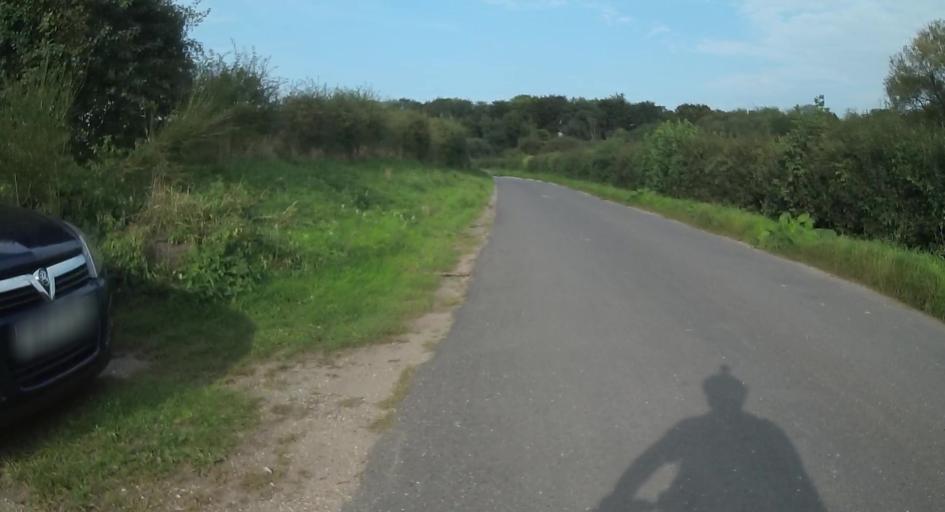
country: GB
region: England
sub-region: Hampshire
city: Kings Worthy
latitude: 51.0731
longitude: -1.1833
